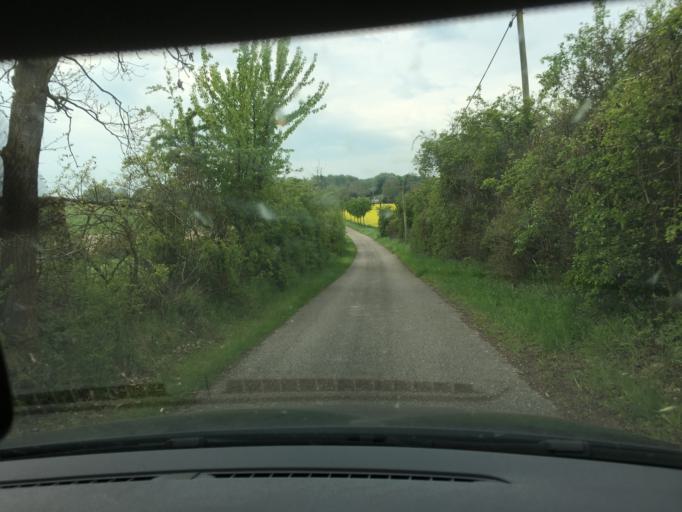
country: DE
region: Mecklenburg-Vorpommern
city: Krakow am See
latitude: 53.6667
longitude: 12.3140
